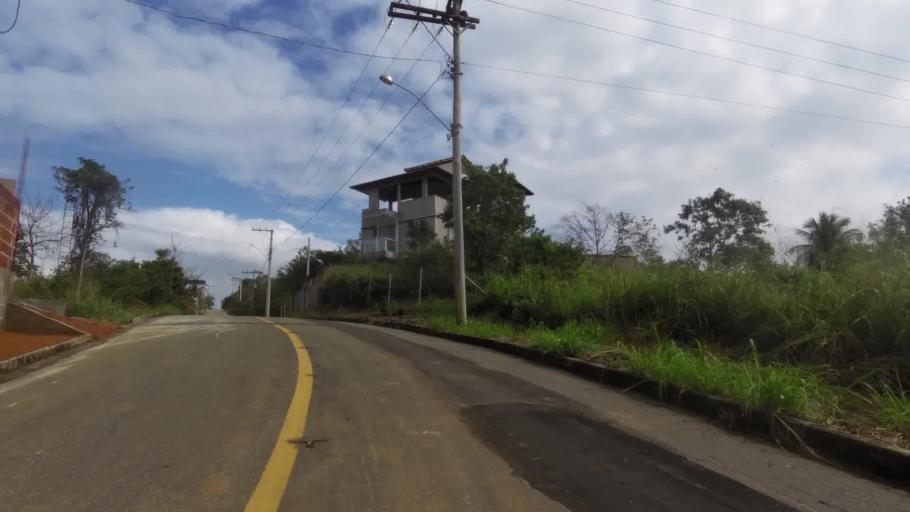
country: BR
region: Espirito Santo
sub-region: Piuma
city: Piuma
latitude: -20.8295
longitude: -40.7004
